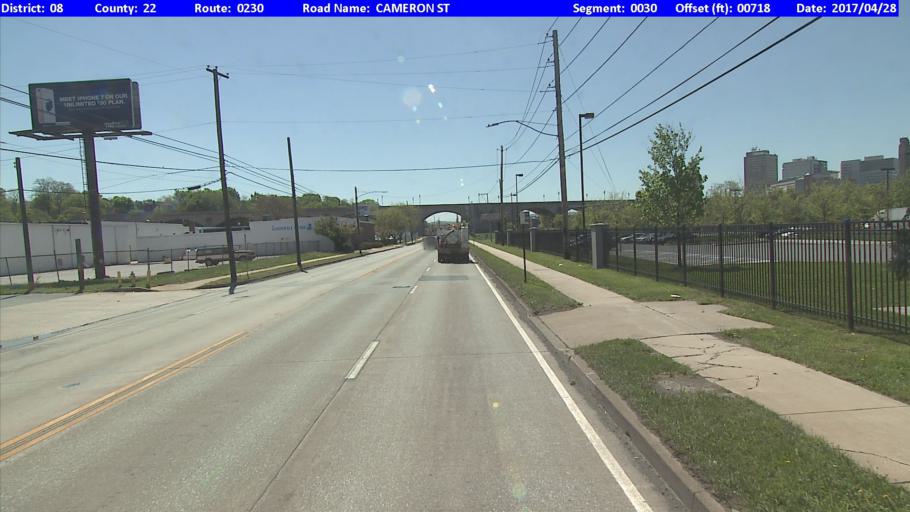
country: US
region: Pennsylvania
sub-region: Dauphin County
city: Harrisburg
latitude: 40.2705
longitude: -76.8767
